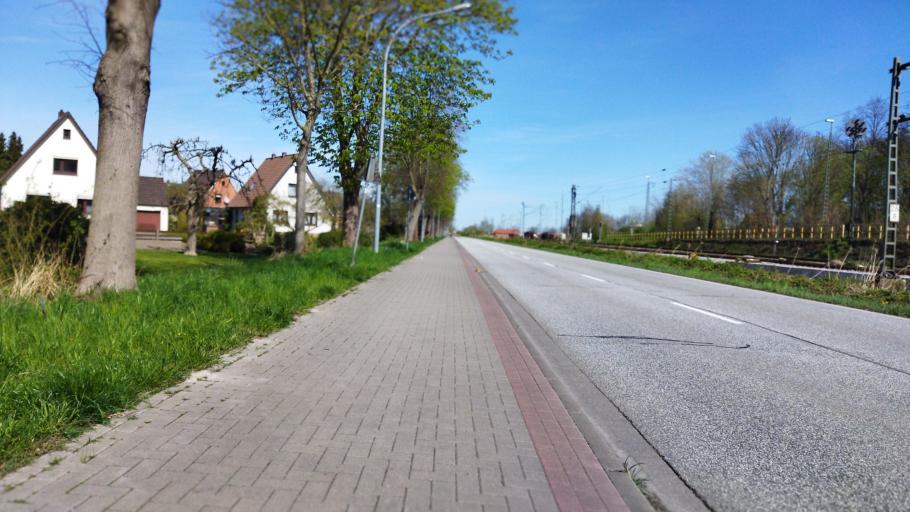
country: DE
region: Lower Saxony
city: Brake (Unterweser)
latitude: 53.3395
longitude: 8.4799
